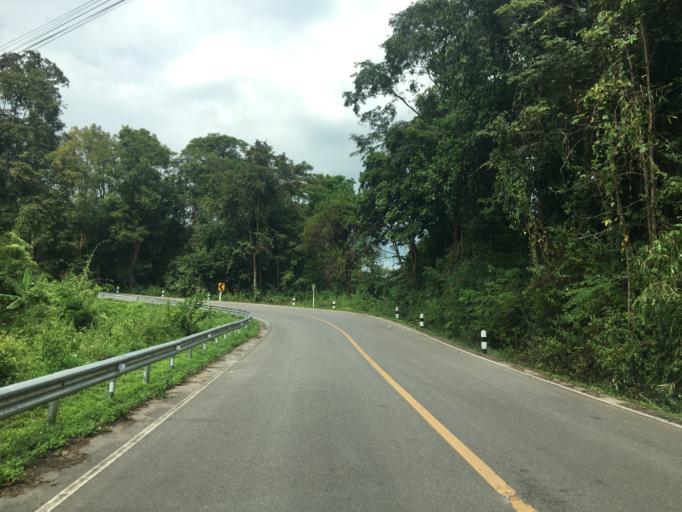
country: TH
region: Nan
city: Ban Luang
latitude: 18.8765
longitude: 100.5431
